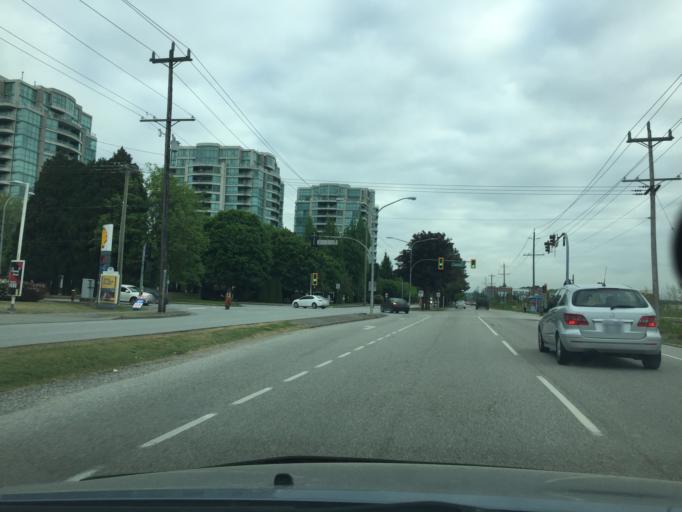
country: CA
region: British Columbia
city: Richmond
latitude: 49.1732
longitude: -123.1246
